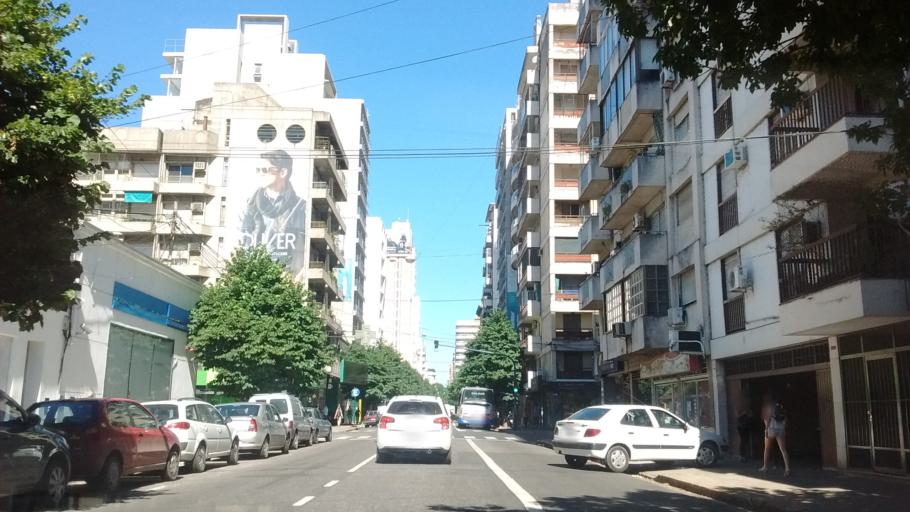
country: AR
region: Santa Fe
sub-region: Departamento de Rosario
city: Rosario
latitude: -32.9431
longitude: -60.6566
